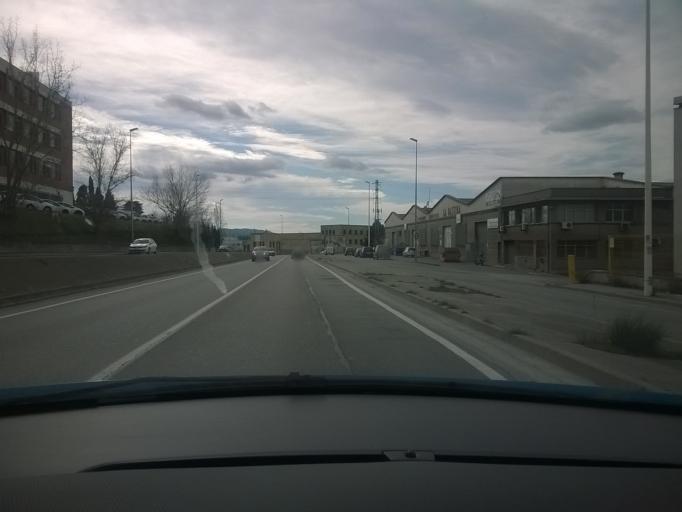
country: ES
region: Catalonia
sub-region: Provincia de Barcelona
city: Rubi
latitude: 41.5080
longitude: 2.0433
